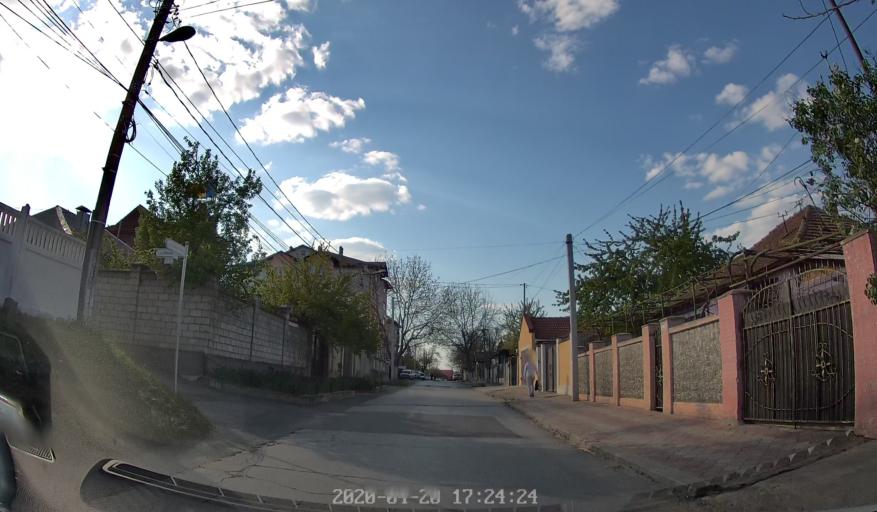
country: MD
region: Chisinau
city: Chisinau
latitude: 46.9903
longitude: 28.8795
